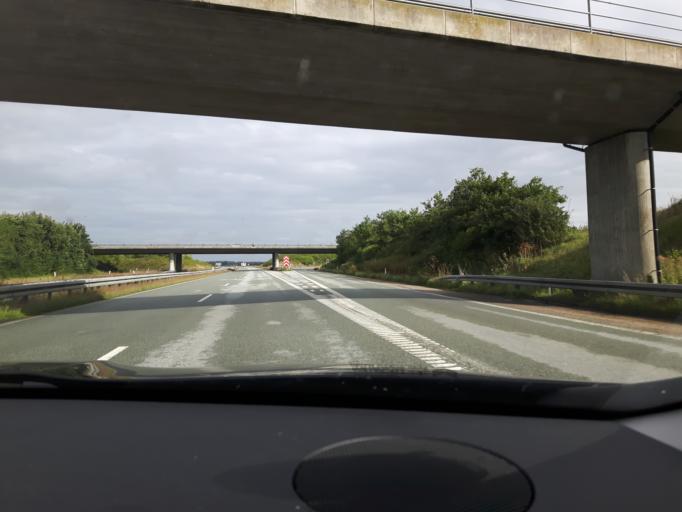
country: DK
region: North Denmark
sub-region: Hjorring Kommune
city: Hjorring
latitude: 57.4548
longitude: 10.0450
